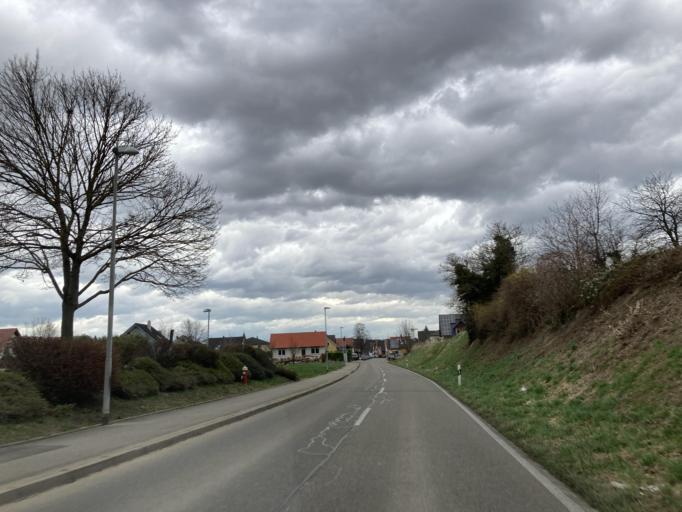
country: DE
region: Baden-Wuerttemberg
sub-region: Freiburg Region
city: Vogtsburg
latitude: 48.1291
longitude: 7.6538
